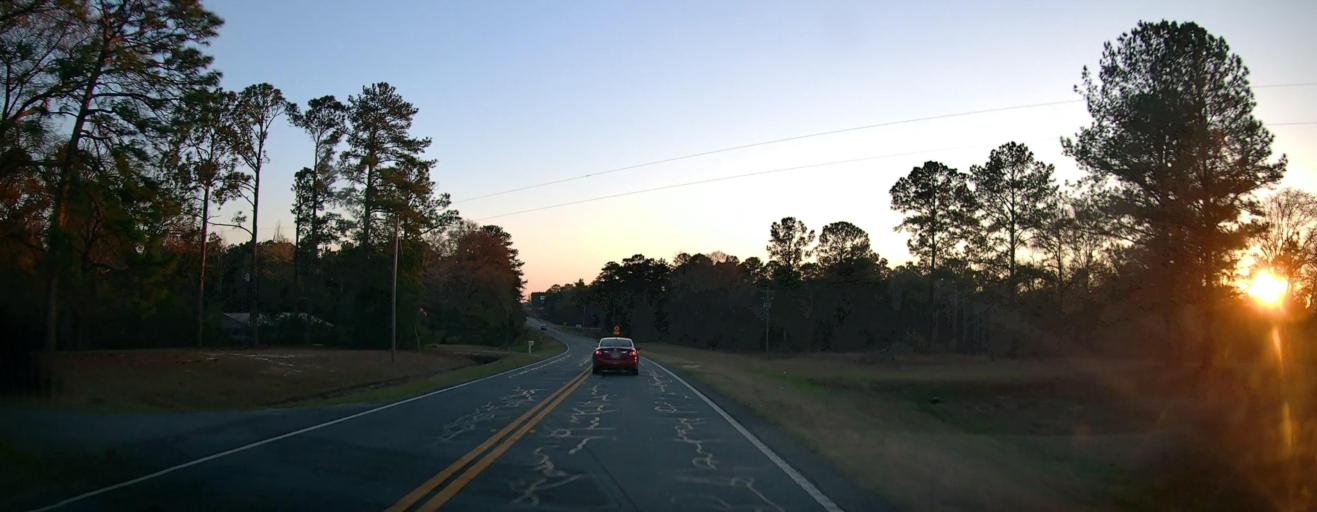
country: US
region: Georgia
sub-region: Dodge County
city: Eastman
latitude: 32.2590
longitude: -83.1379
